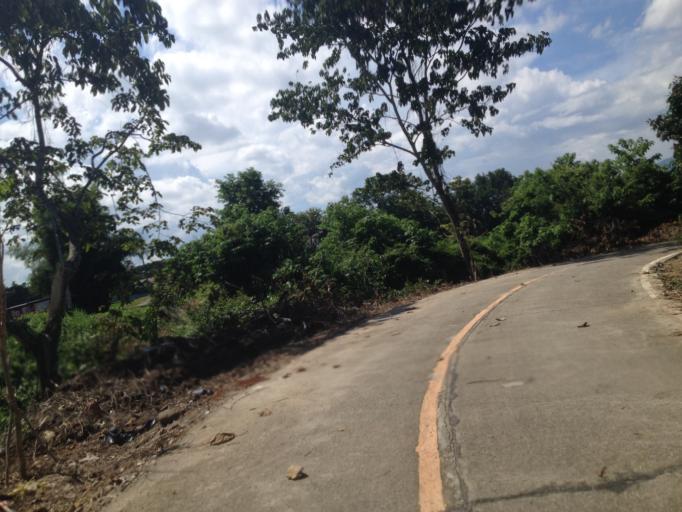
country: TH
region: Chiang Mai
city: Saraphi
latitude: 18.6985
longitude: 98.9800
